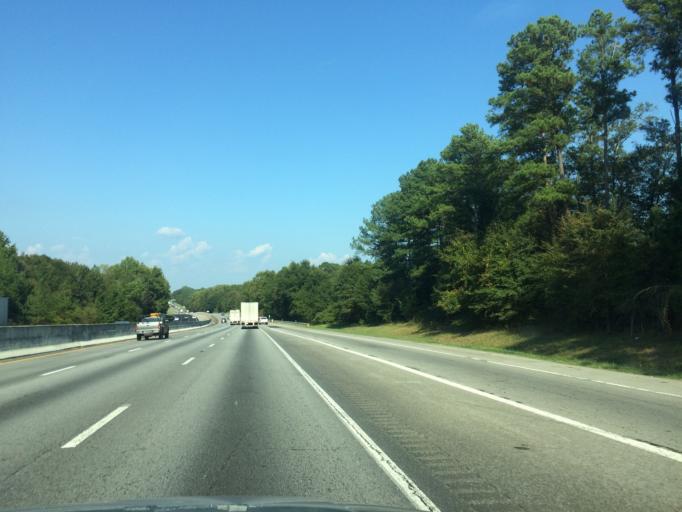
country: US
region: South Carolina
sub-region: Anderson County
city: Northlake
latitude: 34.5806
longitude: -82.6891
